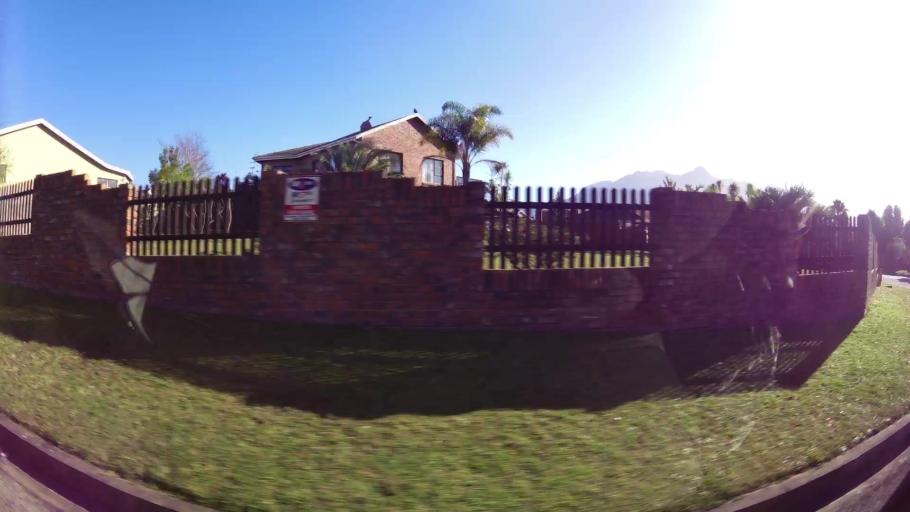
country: ZA
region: Western Cape
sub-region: Eden District Municipality
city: George
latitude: -33.9705
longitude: 22.4412
